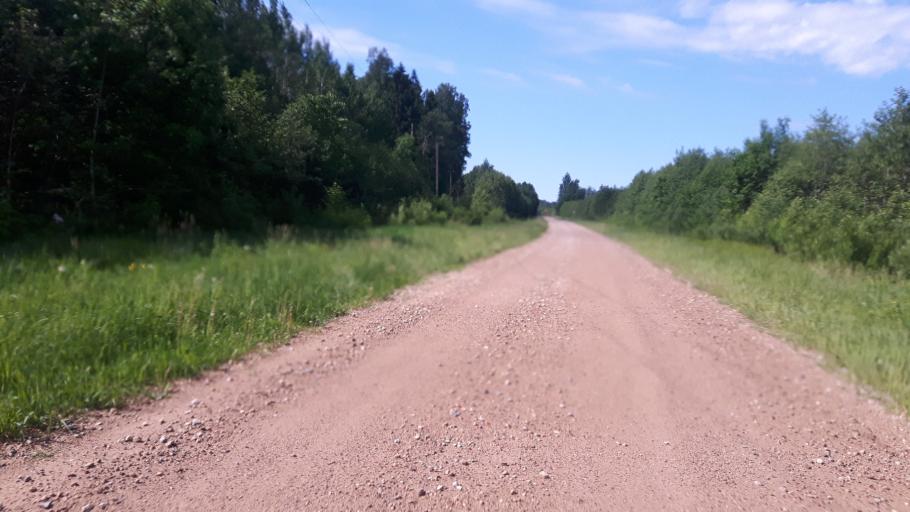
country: EE
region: Paernumaa
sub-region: Vaendra vald (alev)
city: Vandra
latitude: 58.7068
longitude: 25.0360
